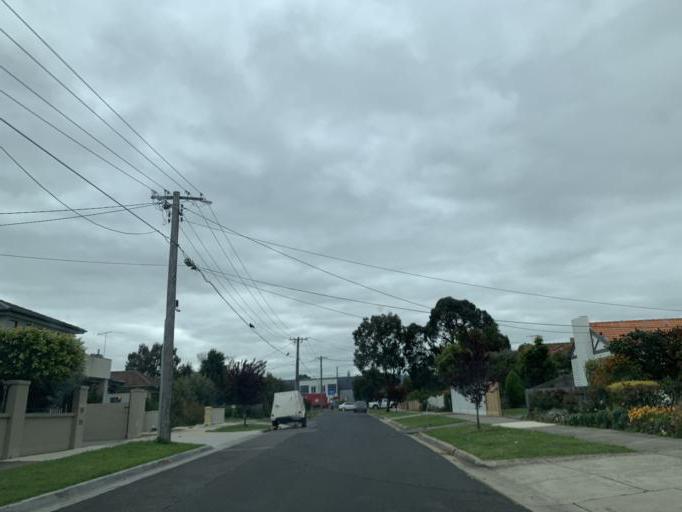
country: AU
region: Victoria
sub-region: Moreland
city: Pascoe Vale South
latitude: -37.7308
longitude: 144.9485
